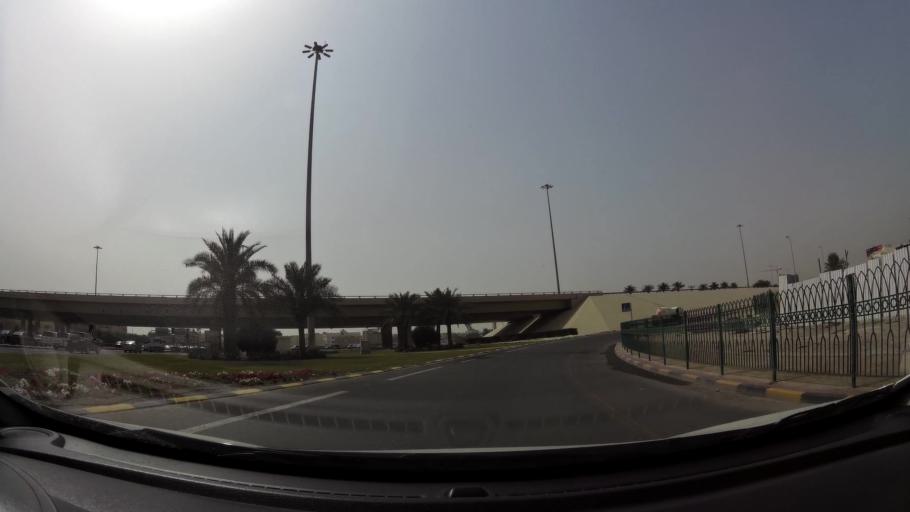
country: BH
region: Manama
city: Jidd Hafs
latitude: 26.2314
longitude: 50.5341
